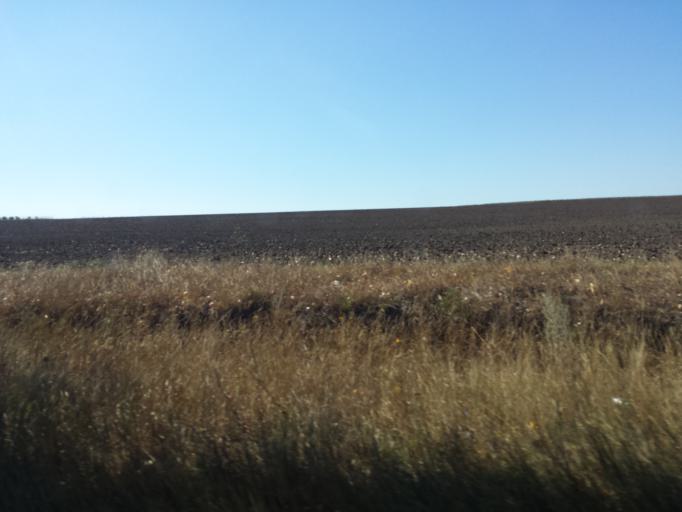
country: RO
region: Tulcea
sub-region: Comuna Frecatei
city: Cataloi
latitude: 45.1100
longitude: 28.7454
